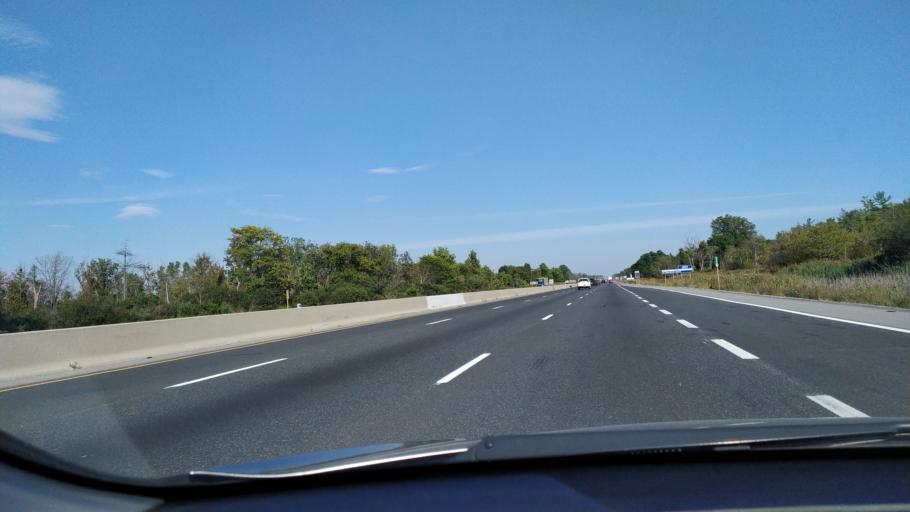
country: CA
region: Ontario
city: Dorchester
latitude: 42.9597
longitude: -81.0525
